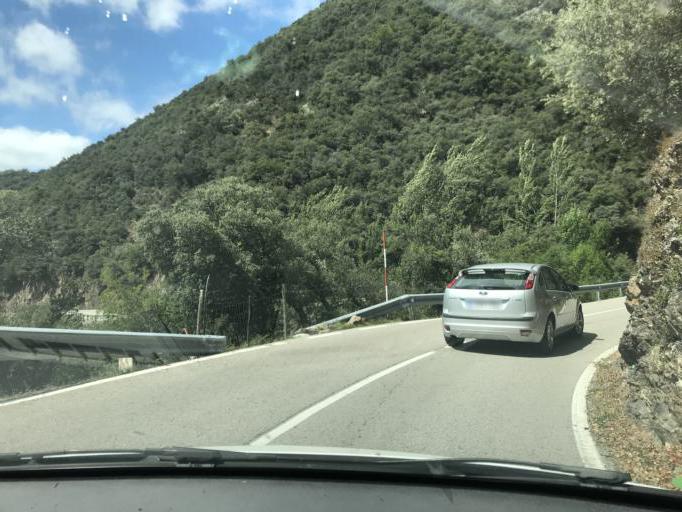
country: ES
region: Cantabria
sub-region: Provincia de Cantabria
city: Cabezon de Liebana
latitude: 43.0781
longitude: -4.5157
